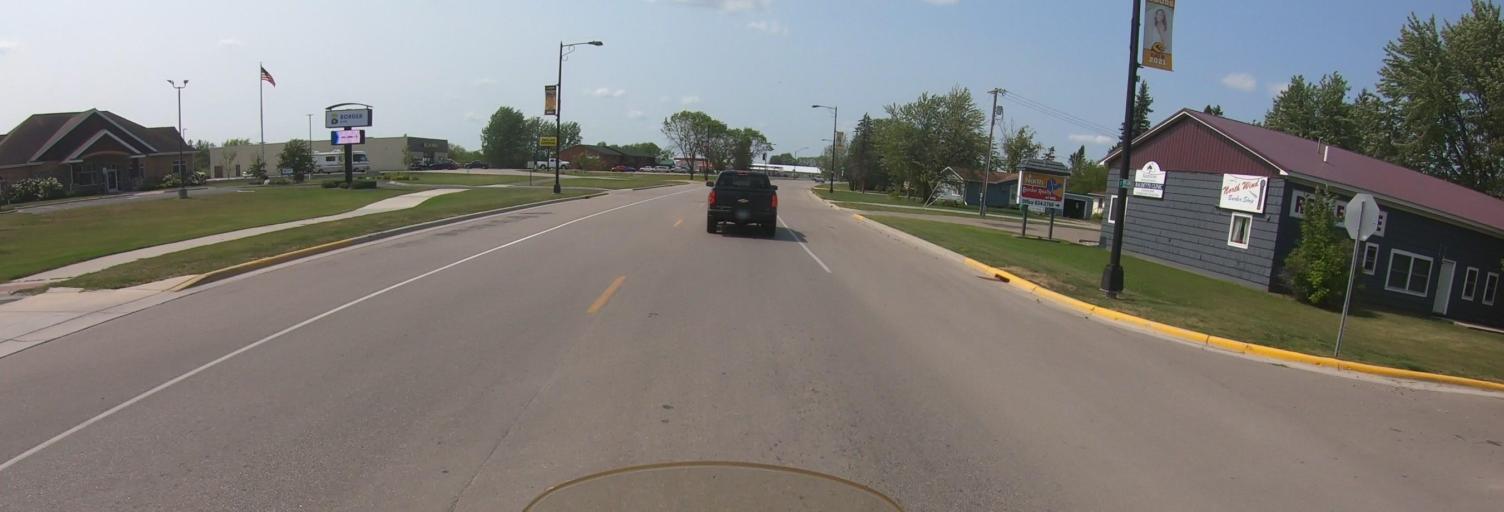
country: US
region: Minnesota
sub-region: Lake of the Woods County
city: Baudette
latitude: 48.7124
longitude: -94.6075
